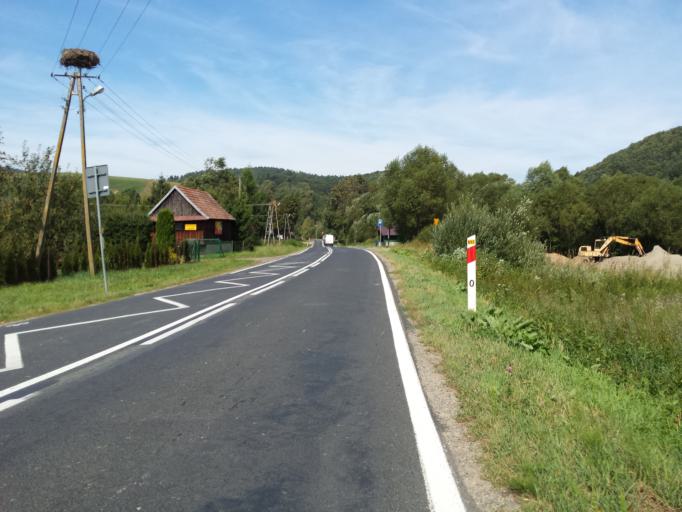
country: PL
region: Subcarpathian Voivodeship
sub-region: Powiat leski
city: Baligrod
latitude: 49.3590
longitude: 22.2806
